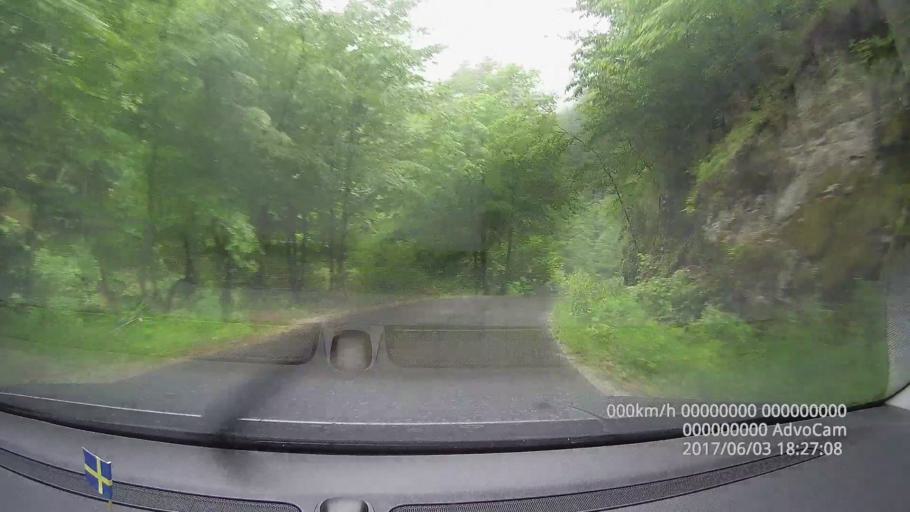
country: RO
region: Gorj
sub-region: Comuna Runcu
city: Dobrita
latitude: 45.1646
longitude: 23.1937
